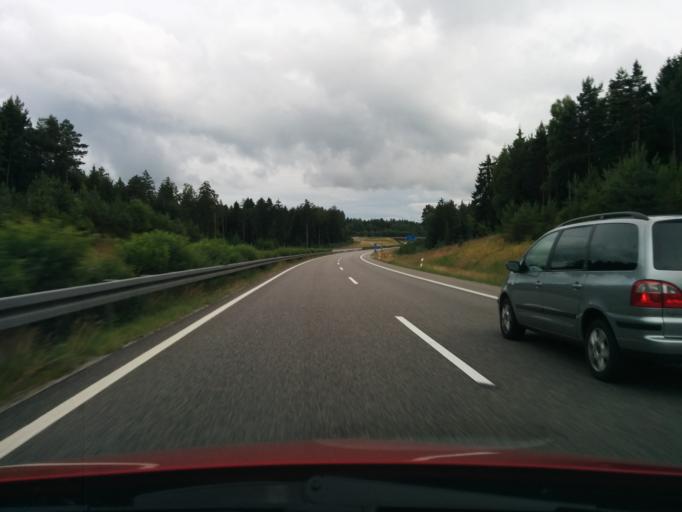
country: DE
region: Thuringia
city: Eisfeld
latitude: 50.3948
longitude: 10.9167
